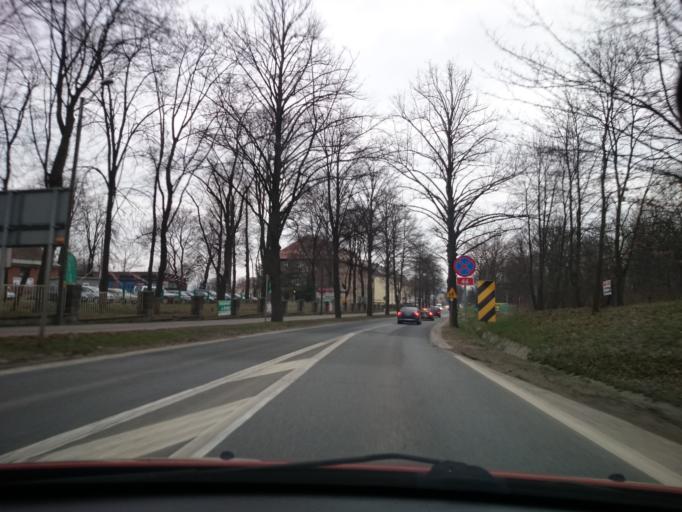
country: PL
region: Opole Voivodeship
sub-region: Powiat nyski
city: Nysa
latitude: 50.4932
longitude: 17.3481
